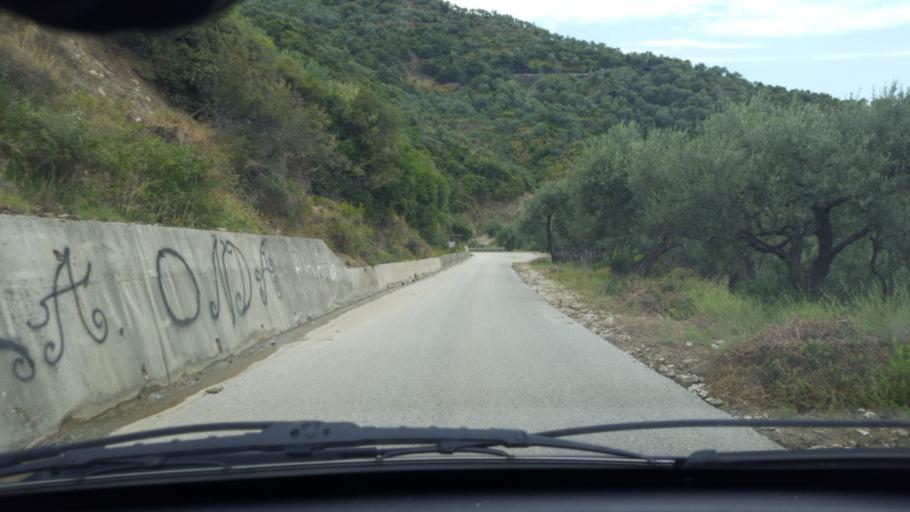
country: AL
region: Vlore
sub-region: Rrethi i Sarandes
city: Lukove
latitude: 39.9866
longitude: 19.9158
